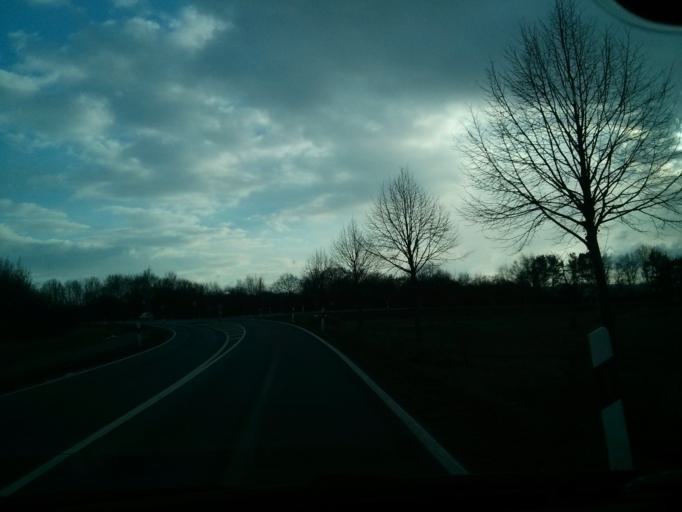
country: DE
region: North Rhine-Westphalia
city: Meckenheim
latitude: 50.6464
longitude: 7.0139
